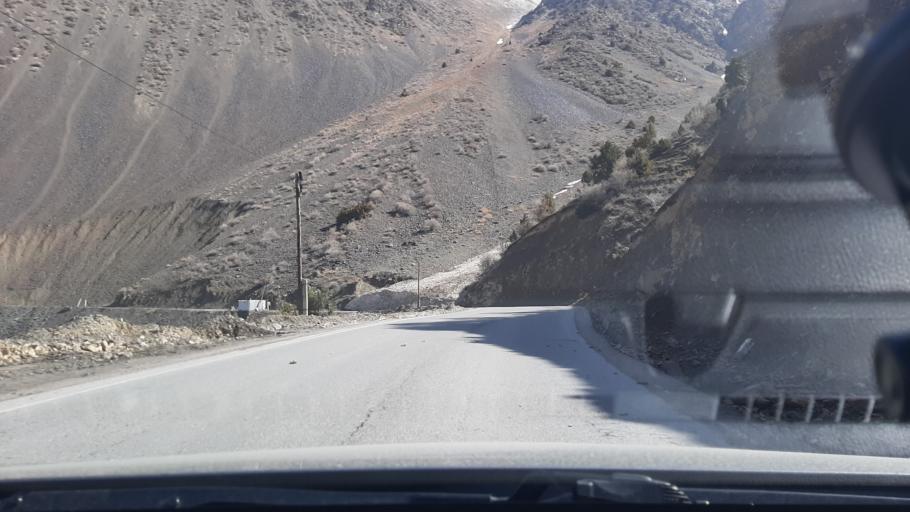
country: TJ
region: Viloyati Sughd
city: Ayni
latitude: 39.4800
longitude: 68.5525
